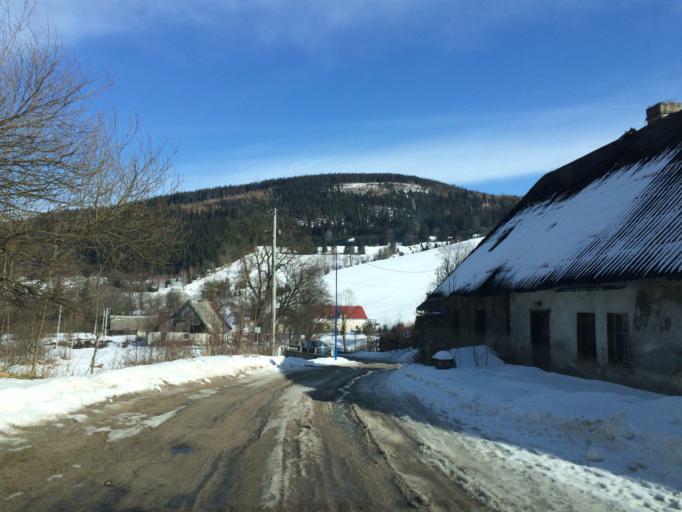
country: CZ
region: Olomoucky
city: Vapenna
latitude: 50.2643
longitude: 16.9971
